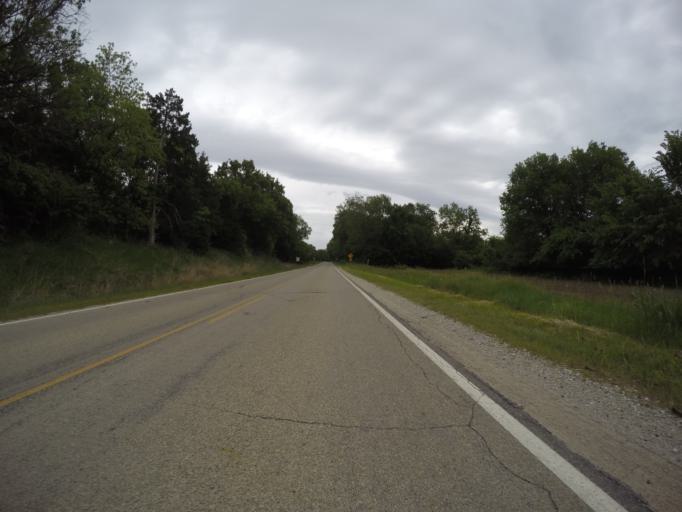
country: US
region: Kansas
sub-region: Pottawatomie County
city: Wamego
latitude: 39.1870
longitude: -96.3316
